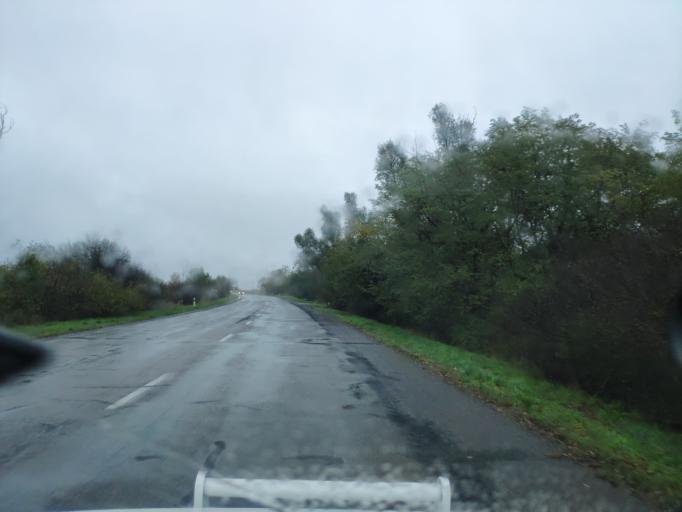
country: SK
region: Kosicky
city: Cierna nad Tisou
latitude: 48.4266
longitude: 21.9968
